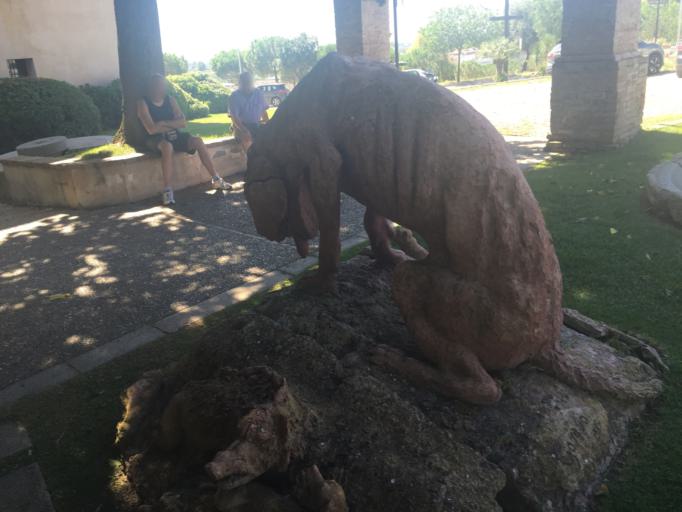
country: IT
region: Basilicate
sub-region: Provincia di Matera
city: Policoro
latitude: 40.2165
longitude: 16.6803
